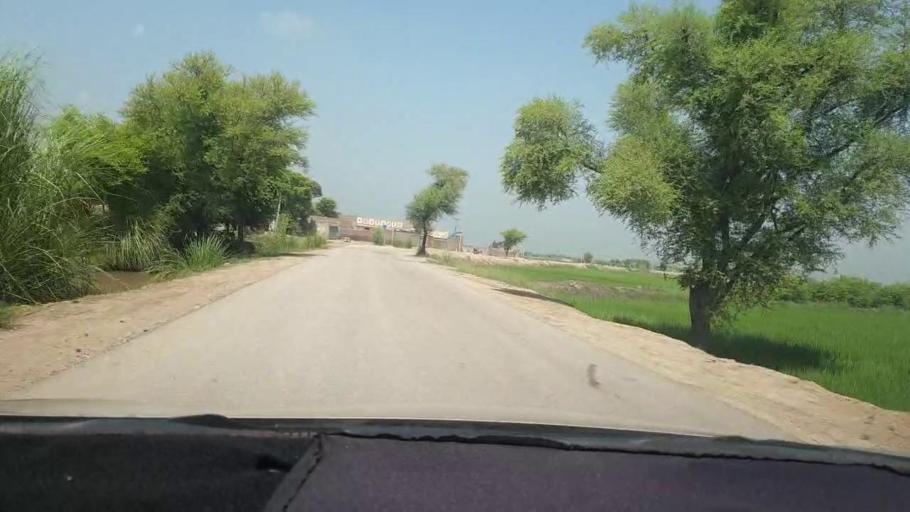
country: PK
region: Sindh
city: Miro Khan
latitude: 27.7726
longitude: 68.0597
